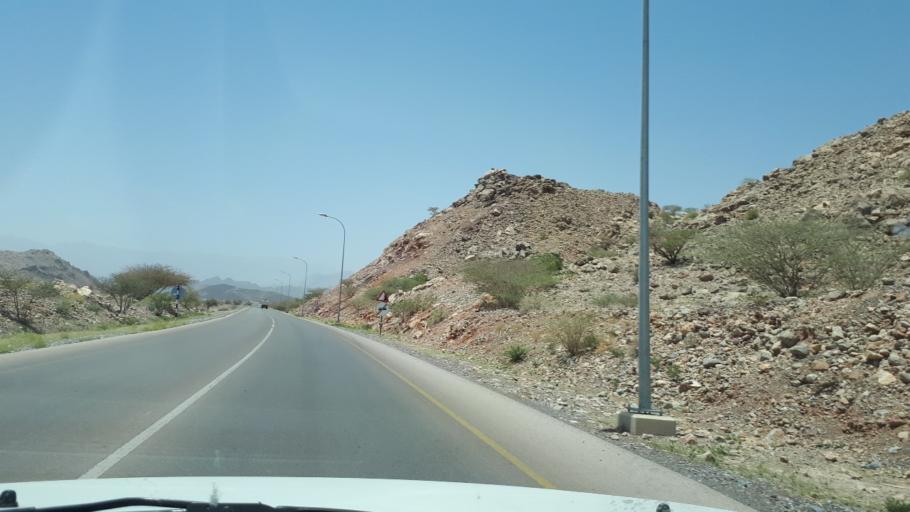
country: OM
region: Muhafazat ad Dakhiliyah
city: Bahla'
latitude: 23.0518
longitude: 57.3061
